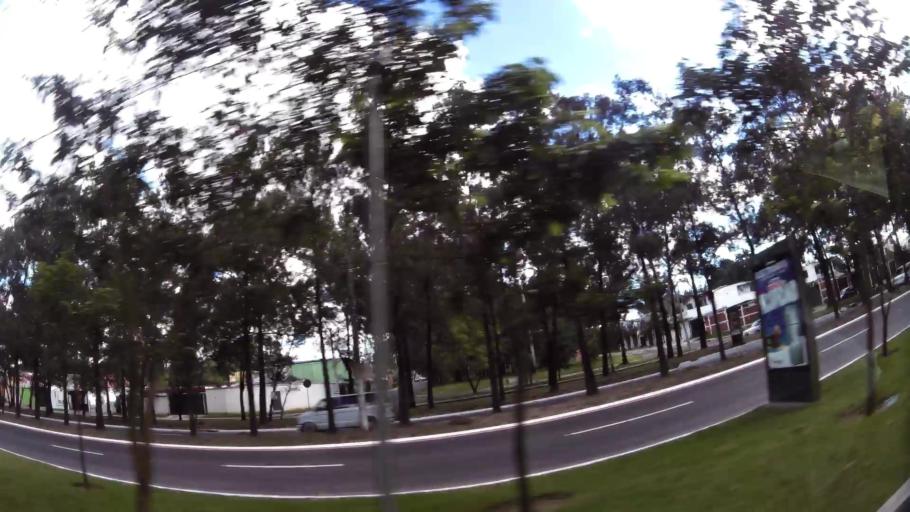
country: GT
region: Guatemala
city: Mixco
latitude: 14.6057
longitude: -90.5595
